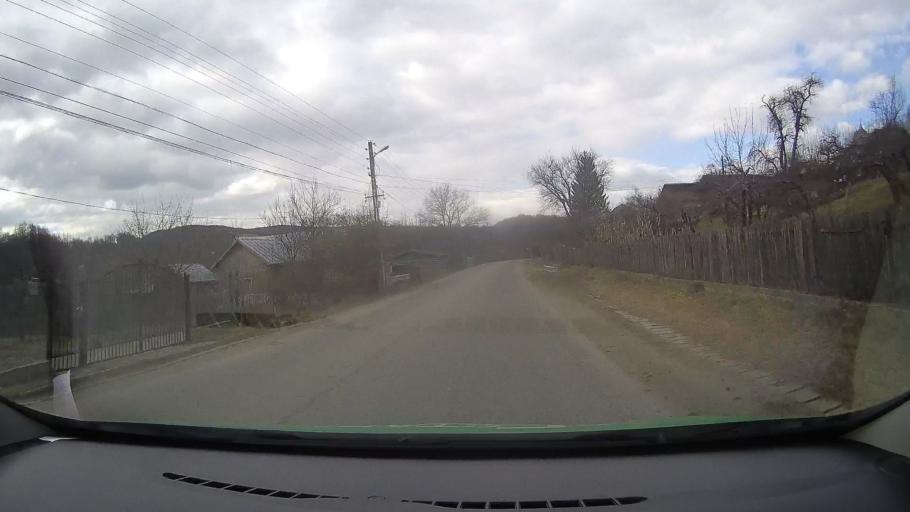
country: RO
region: Dambovita
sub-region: Comuna Valea Lunga
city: Valea Lunga-Cricov
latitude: 45.0656
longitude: 25.5681
